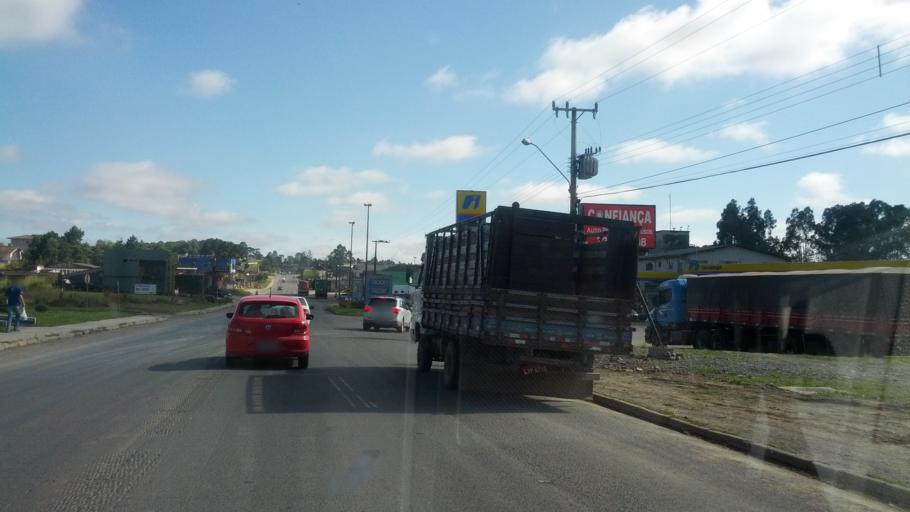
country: BR
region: Santa Catarina
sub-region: Otacilio Costa
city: Otacilio Costa
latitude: -27.4945
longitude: -50.1208
